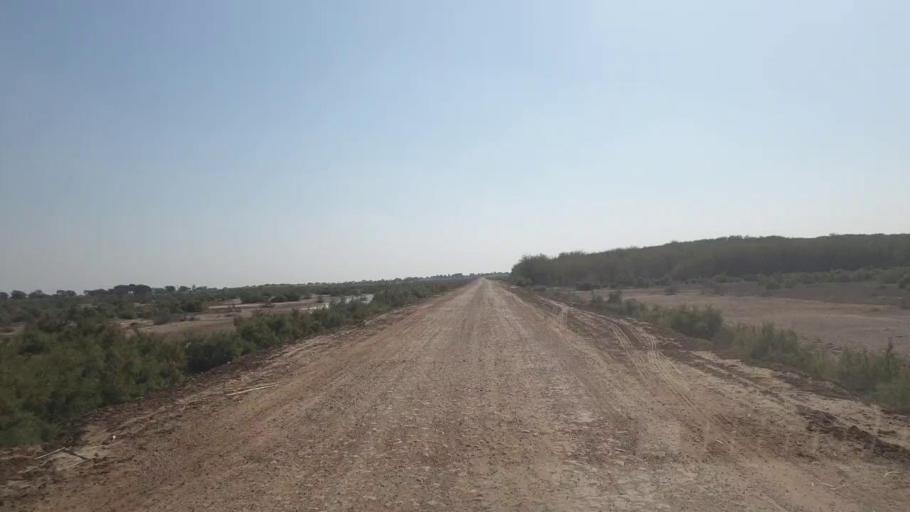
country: PK
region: Sindh
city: Chambar
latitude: 25.3287
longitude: 68.7399
